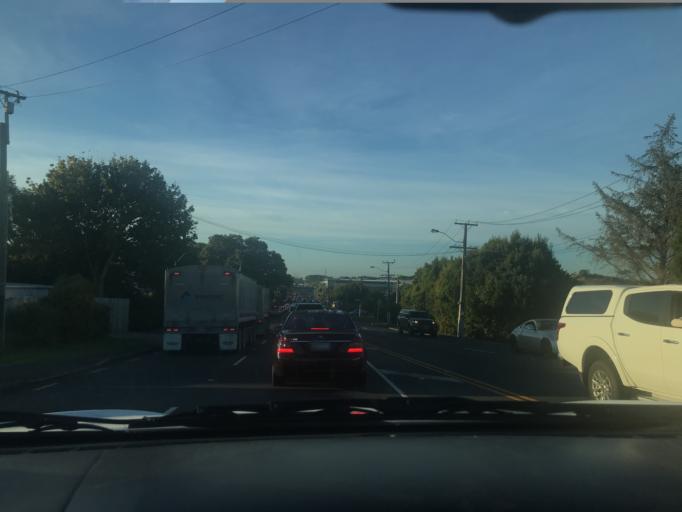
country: NZ
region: Auckland
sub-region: Auckland
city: Tamaki
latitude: -36.9106
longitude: 174.8378
